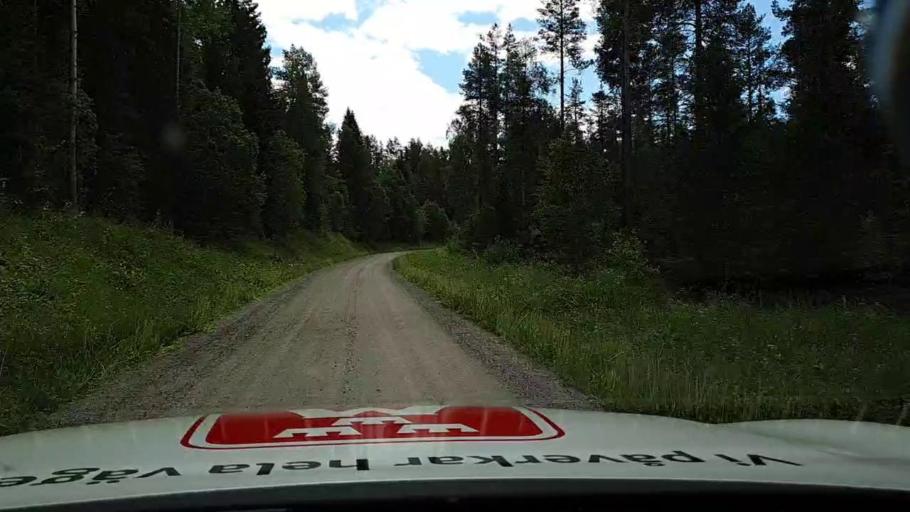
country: SE
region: Jaemtland
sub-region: Braecke Kommun
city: Braecke
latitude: 62.7569
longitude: 15.5022
